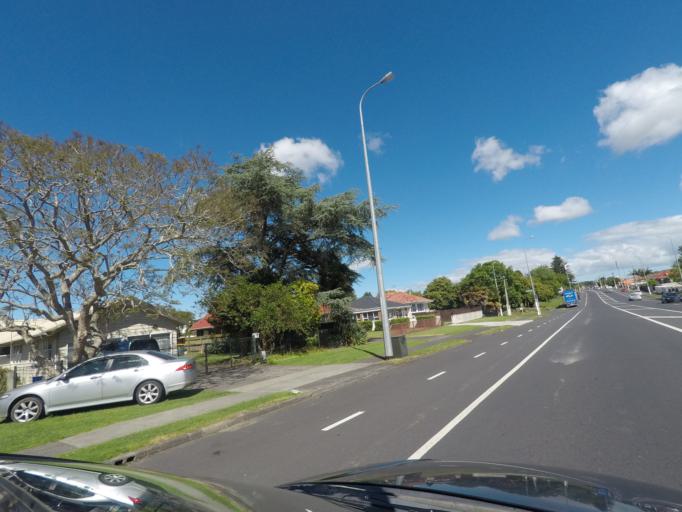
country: NZ
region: Auckland
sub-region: Auckland
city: Manukau City
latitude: -36.9791
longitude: 174.8738
